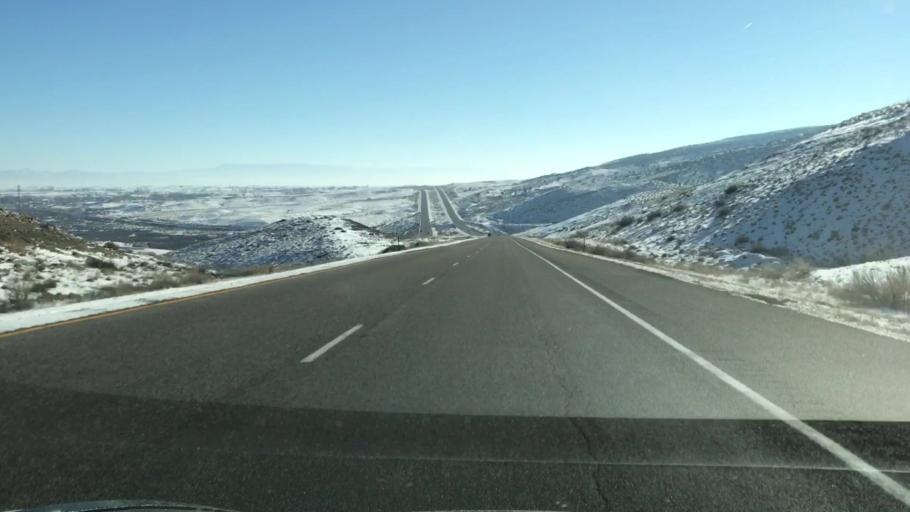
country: US
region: Colorado
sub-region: Mesa County
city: Loma
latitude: 39.2272
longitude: -108.9005
